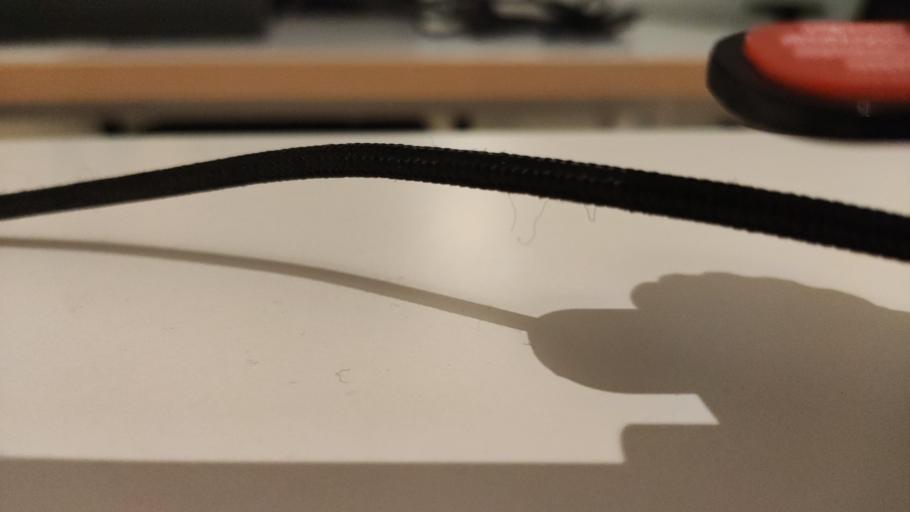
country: RU
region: Moskovskaya
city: Budenovetc
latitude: 56.3936
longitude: 37.6321
